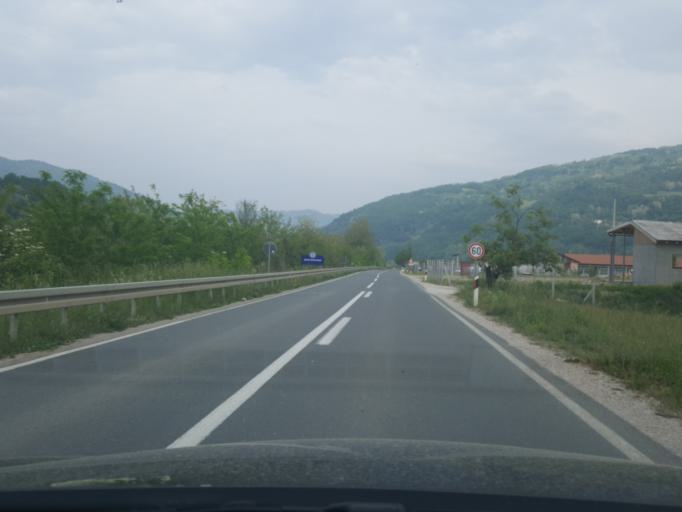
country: RS
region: Central Serbia
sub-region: Zlatiborski Okrug
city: Bajina Basta
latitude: 44.0005
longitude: 19.5738
